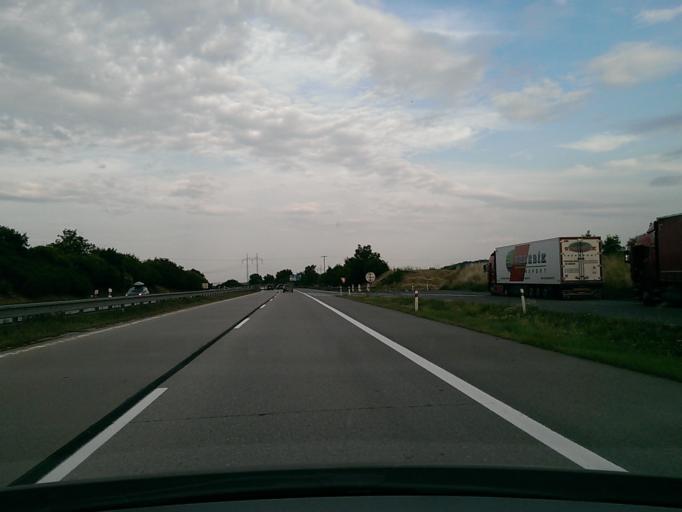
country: CZ
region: South Moravian
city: Troubsko
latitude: 49.1732
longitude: 16.5139
